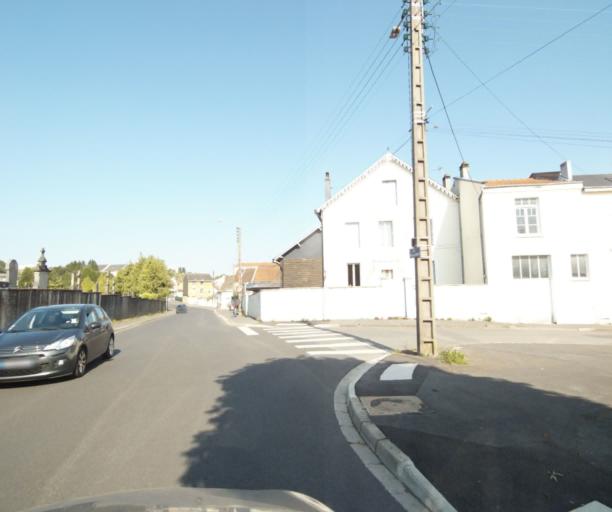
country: FR
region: Champagne-Ardenne
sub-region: Departement des Ardennes
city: Charleville-Mezieres
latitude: 49.7767
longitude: 4.7086
